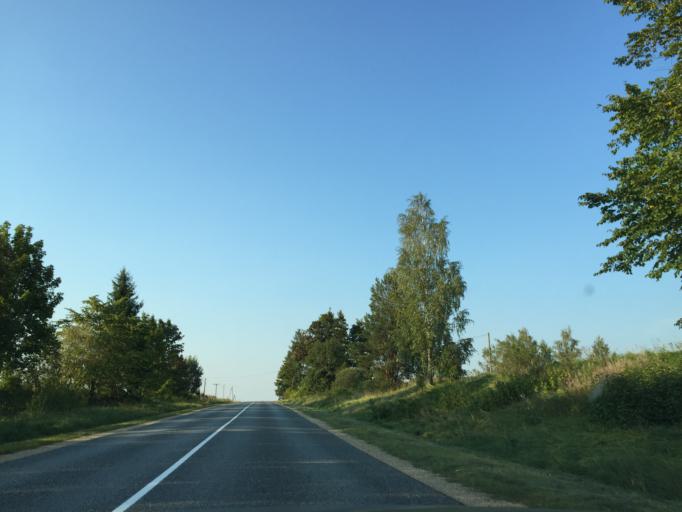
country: LV
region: Limbazu Rajons
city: Limbazi
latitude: 57.5702
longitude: 24.7694
